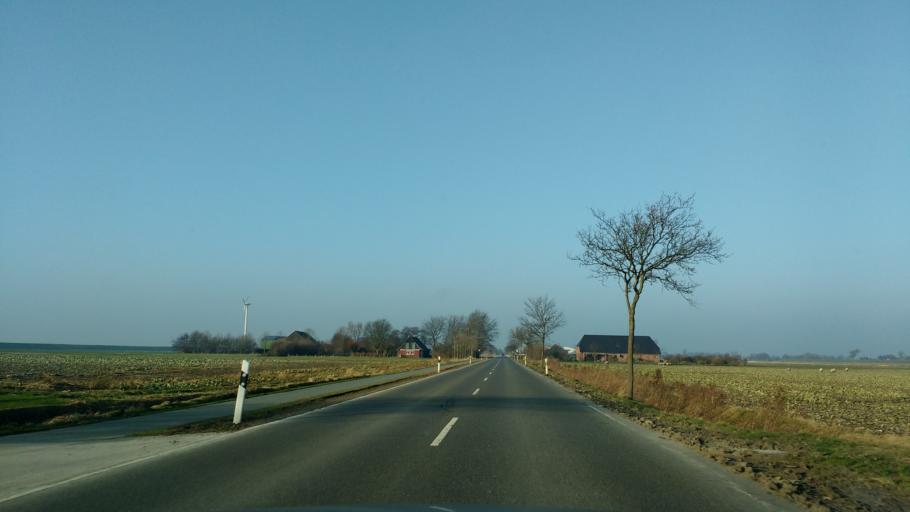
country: DE
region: Schleswig-Holstein
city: Friedrichskoog
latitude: 53.9919
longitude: 8.9022
